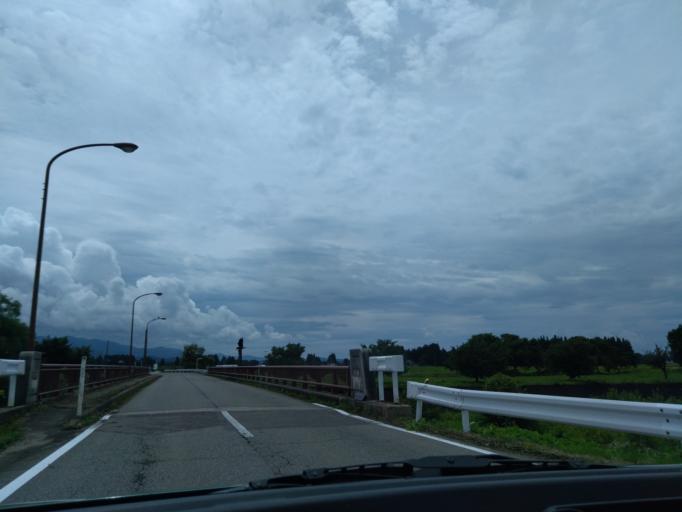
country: JP
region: Akita
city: Kakunodatemachi
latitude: 39.5344
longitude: 140.6410
